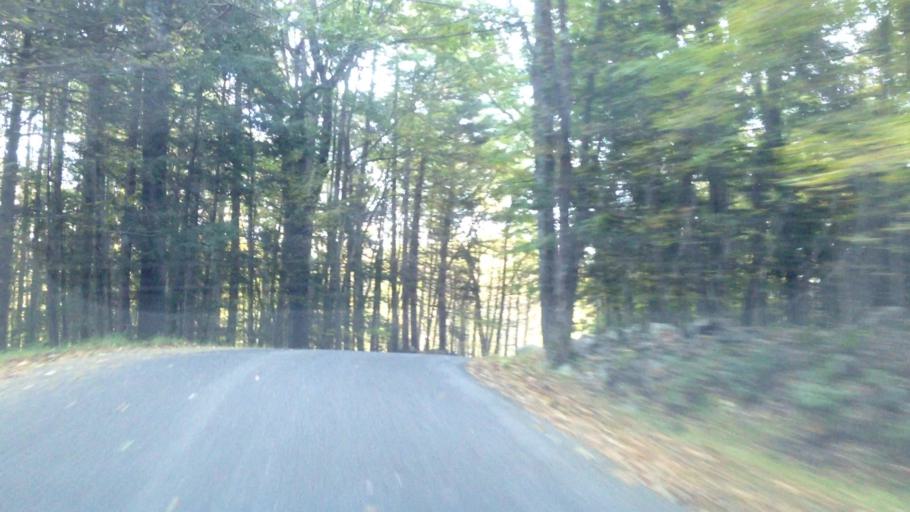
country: US
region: New York
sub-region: Ulster County
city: Port Ewen
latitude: 41.8527
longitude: -74.0101
